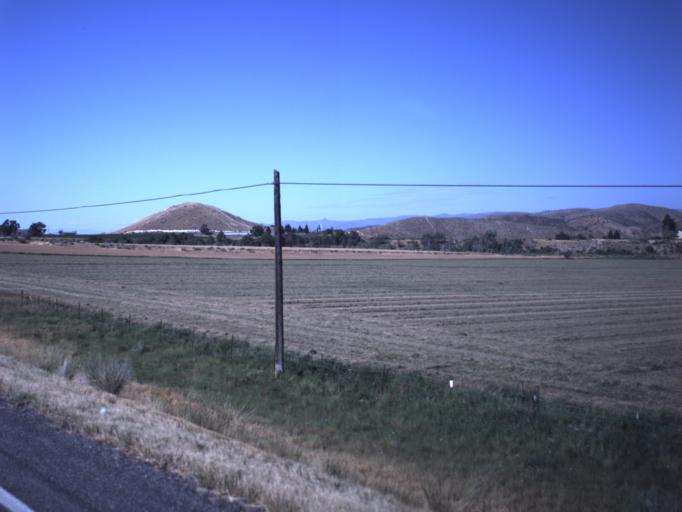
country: US
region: Utah
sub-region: Sanpete County
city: Manti
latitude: 39.2018
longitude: -111.6918
